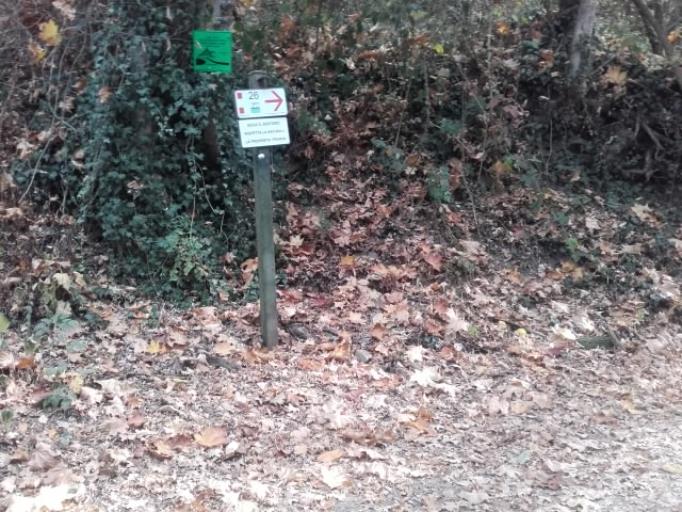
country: IT
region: Piedmont
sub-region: Provincia di Torino
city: San Mauro Torinese
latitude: 45.0751
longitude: 7.7637
